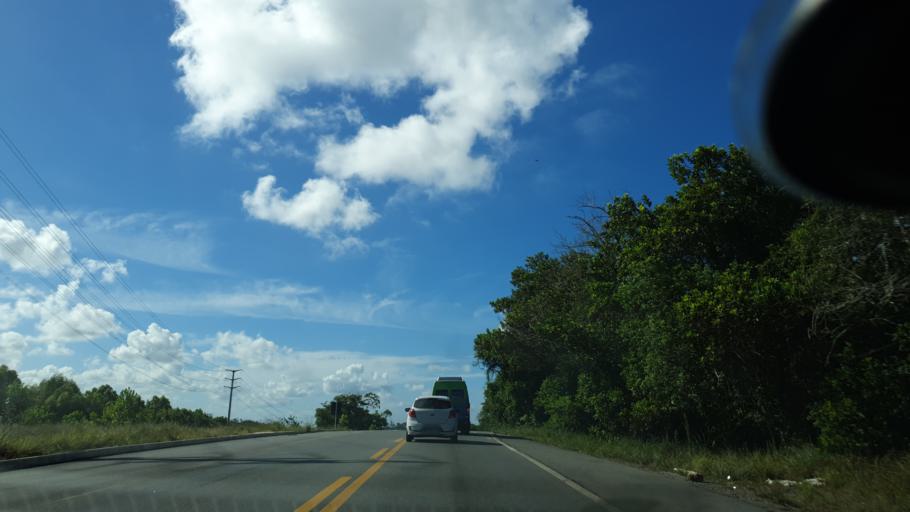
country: BR
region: Bahia
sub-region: Camacari
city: Camacari
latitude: -12.6913
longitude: -38.2255
